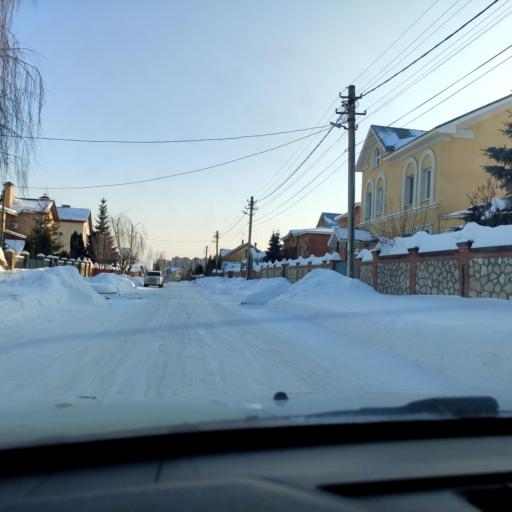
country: RU
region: Samara
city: Novosemeykino
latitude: 53.3234
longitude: 50.2862
